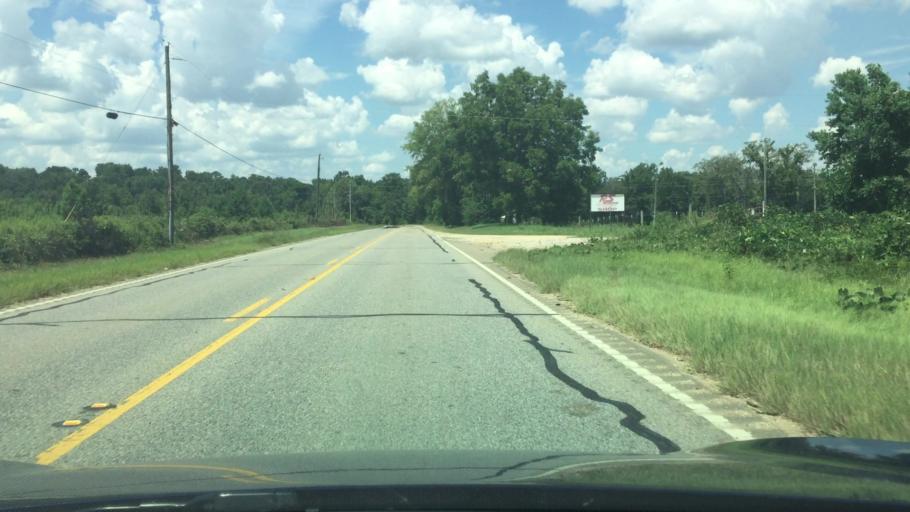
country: US
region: Alabama
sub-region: Montgomery County
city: Pike Road
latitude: 32.3689
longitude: -86.0278
